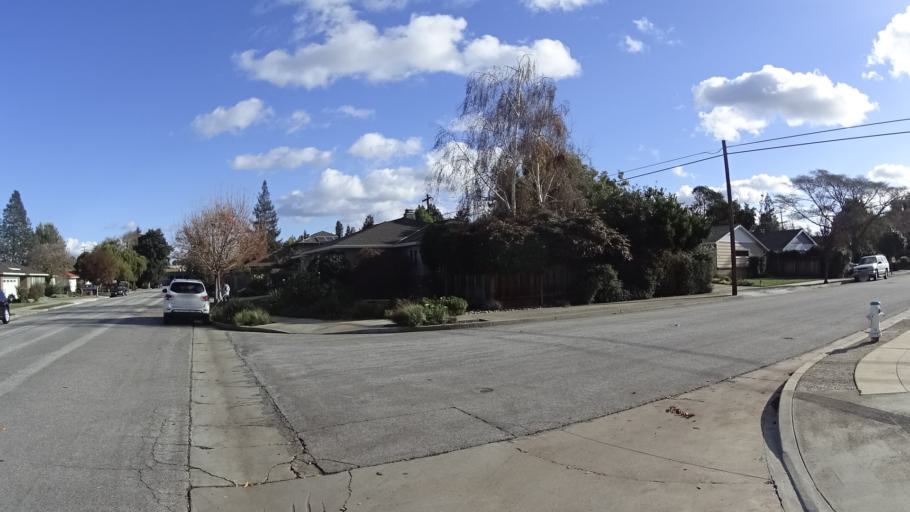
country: US
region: California
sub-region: Santa Clara County
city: Sunnyvale
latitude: 37.3737
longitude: -122.0417
